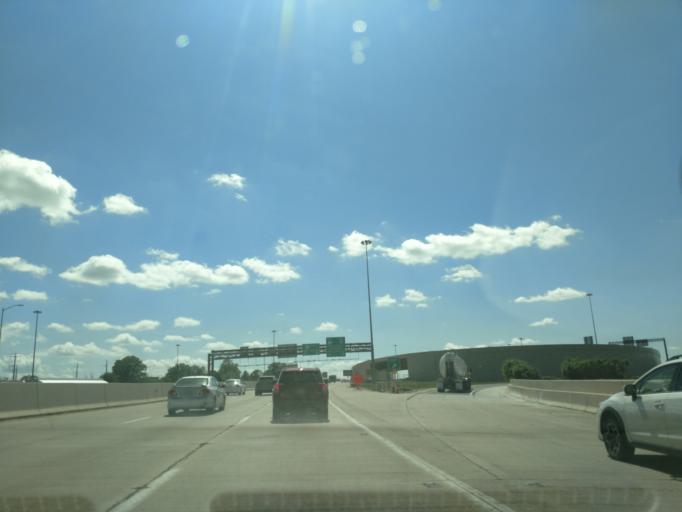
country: US
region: Pennsylvania
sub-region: Montgomery County
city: King of Prussia
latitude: 40.0849
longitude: -75.3885
